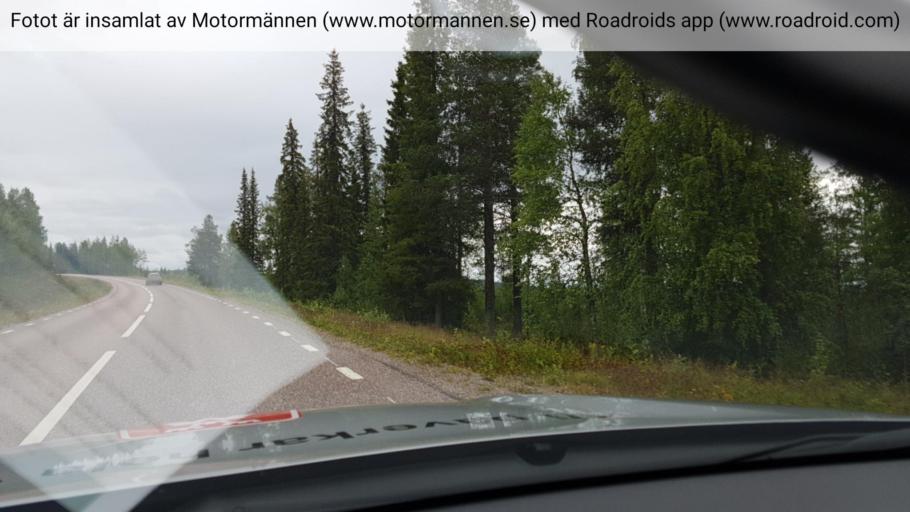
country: SE
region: Norrbotten
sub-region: Gallivare Kommun
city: Gaellivare
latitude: 67.0467
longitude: 21.6177
